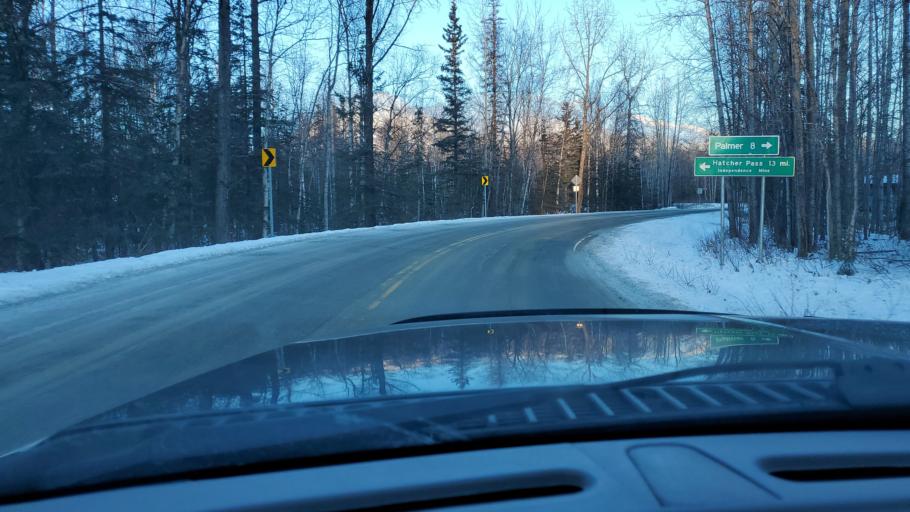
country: US
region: Alaska
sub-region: Matanuska-Susitna Borough
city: Fishhook
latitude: 61.6882
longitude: -149.2439
